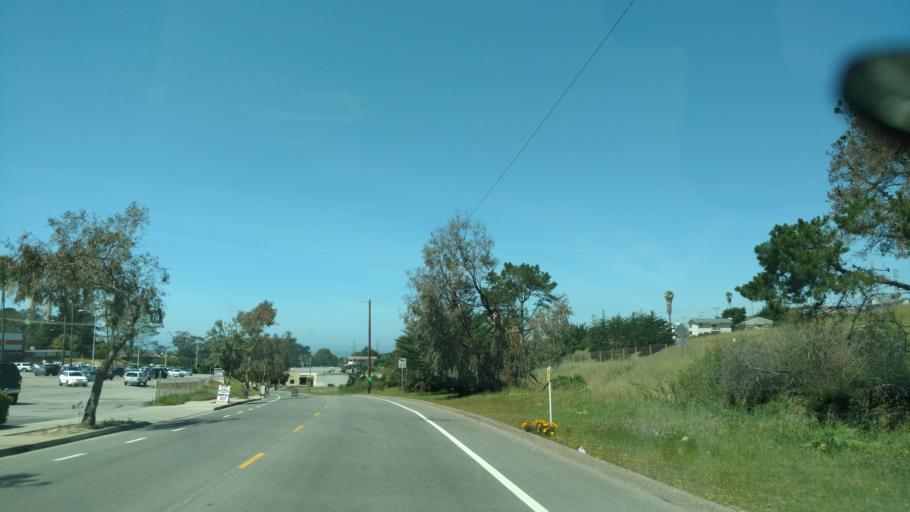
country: US
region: California
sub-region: San Luis Obispo County
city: Morro Bay
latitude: 35.3697
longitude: -120.8450
